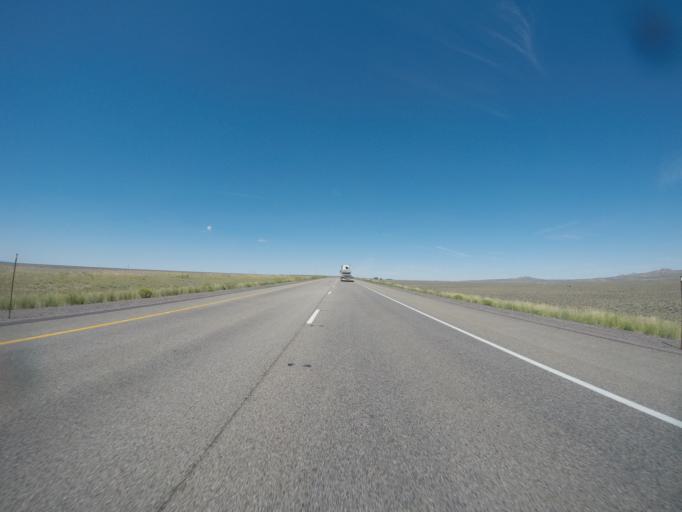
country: US
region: Wyoming
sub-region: Carbon County
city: Saratoga
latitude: 41.7422
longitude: -106.8019
